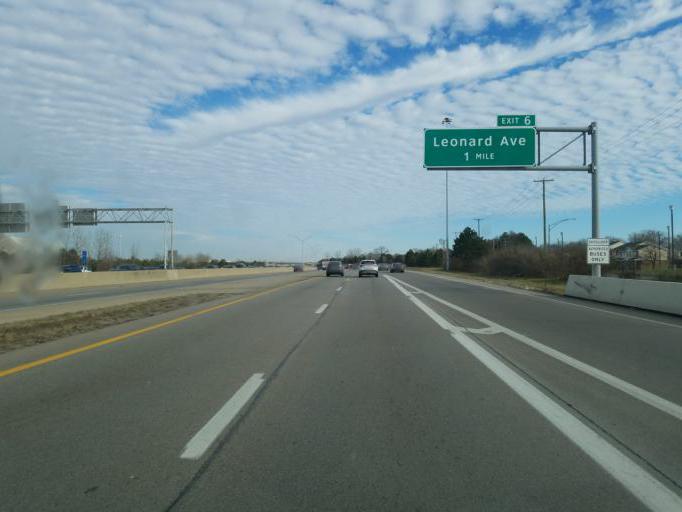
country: US
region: Ohio
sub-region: Franklin County
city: Columbus
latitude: 39.9782
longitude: -82.9772
